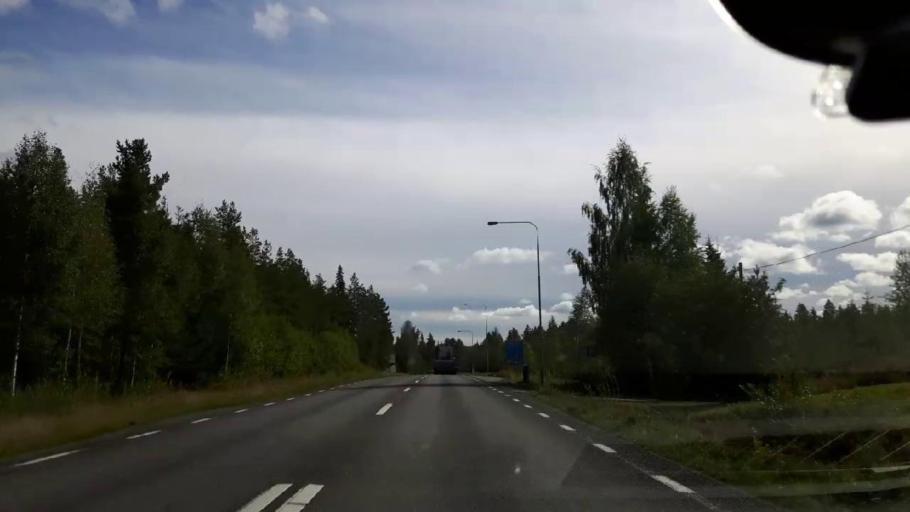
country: SE
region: Jaemtland
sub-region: Braecke Kommun
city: Braecke
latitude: 63.1755
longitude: 15.5333
